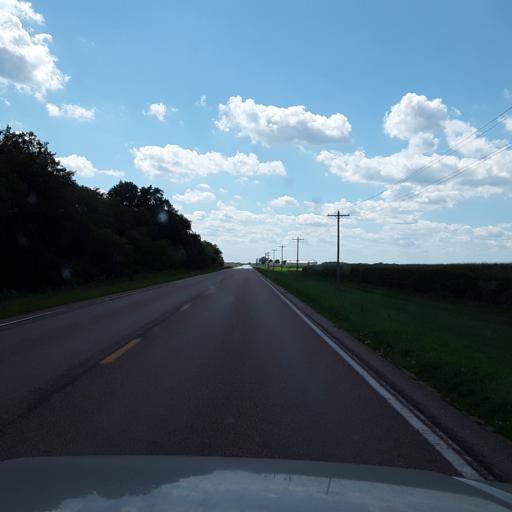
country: US
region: Nebraska
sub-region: Merrick County
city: Central City
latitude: 41.1910
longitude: -98.0248
